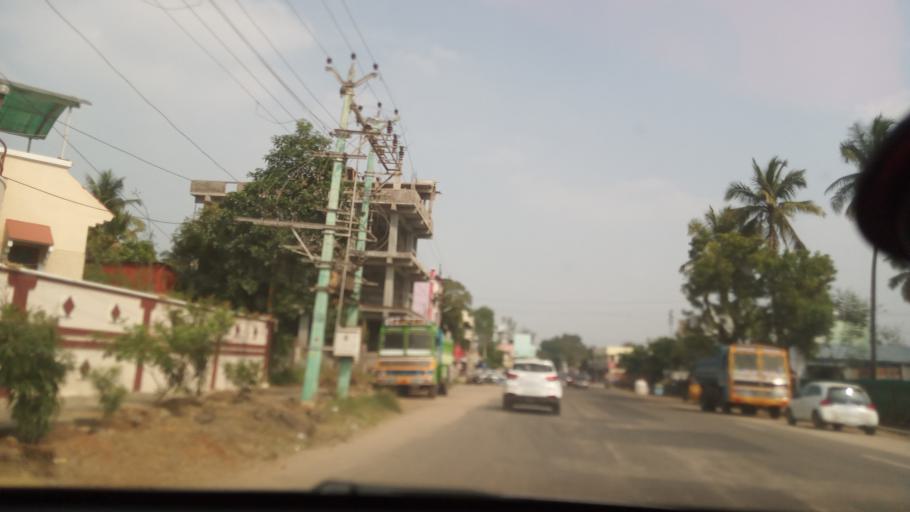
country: IN
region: Tamil Nadu
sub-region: Coimbatore
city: Perur
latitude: 11.0248
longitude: 76.9000
